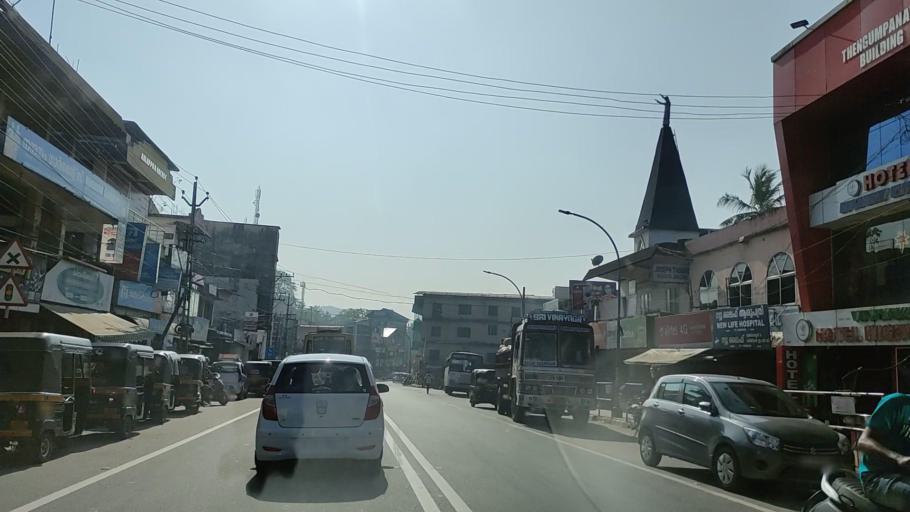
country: IN
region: Kerala
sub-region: Kollam
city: Punalur
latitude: 8.8990
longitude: 76.8594
